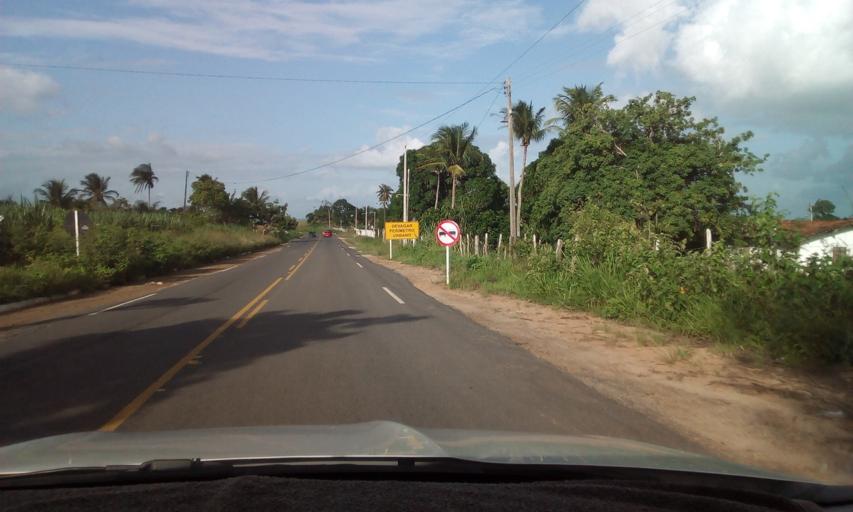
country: BR
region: Paraiba
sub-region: Mamanguape
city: Mamanguape
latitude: -6.8150
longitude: -35.2117
